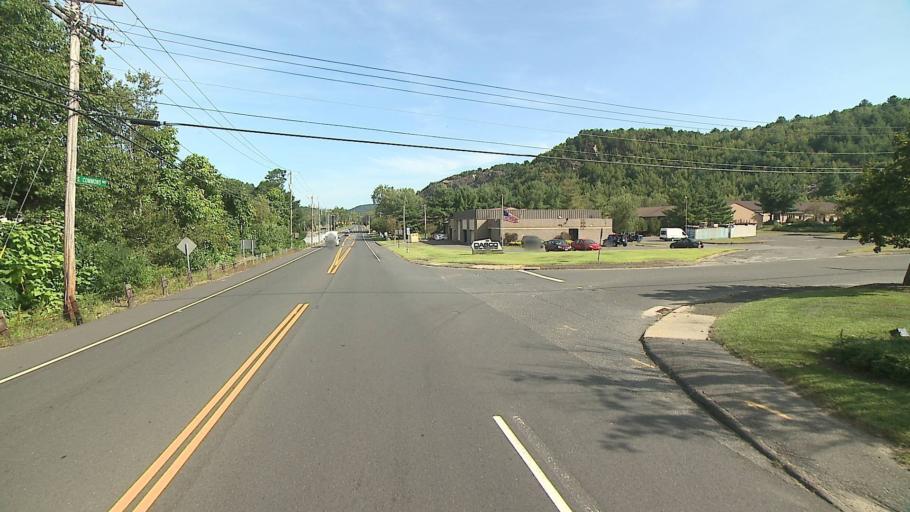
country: US
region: Connecticut
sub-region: Litchfield County
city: Oakville
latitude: 41.5962
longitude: -73.0574
